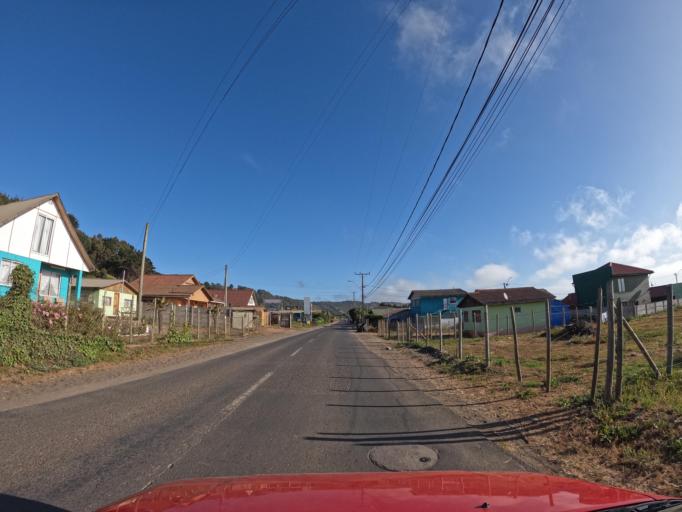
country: CL
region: Maule
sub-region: Provincia de Talca
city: Constitucion
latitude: -34.9235
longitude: -72.1796
